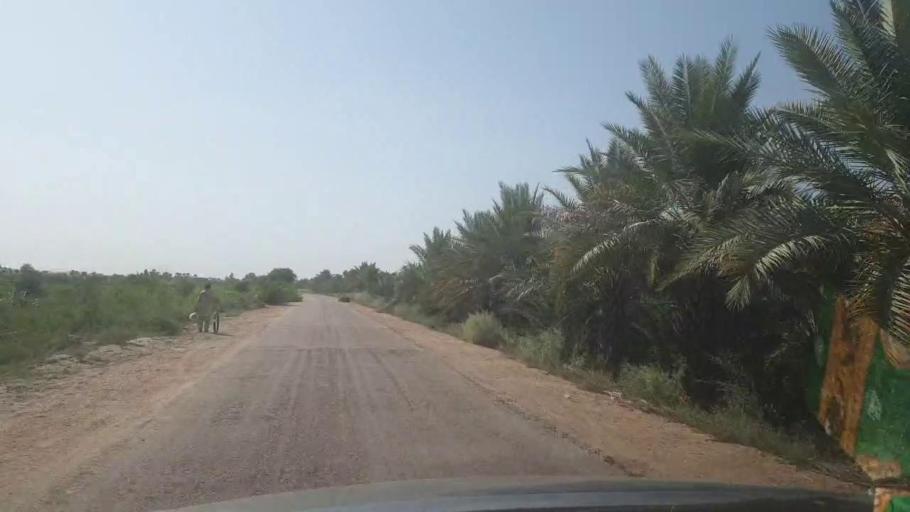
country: PK
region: Sindh
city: Rohri
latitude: 27.4651
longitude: 69.0388
